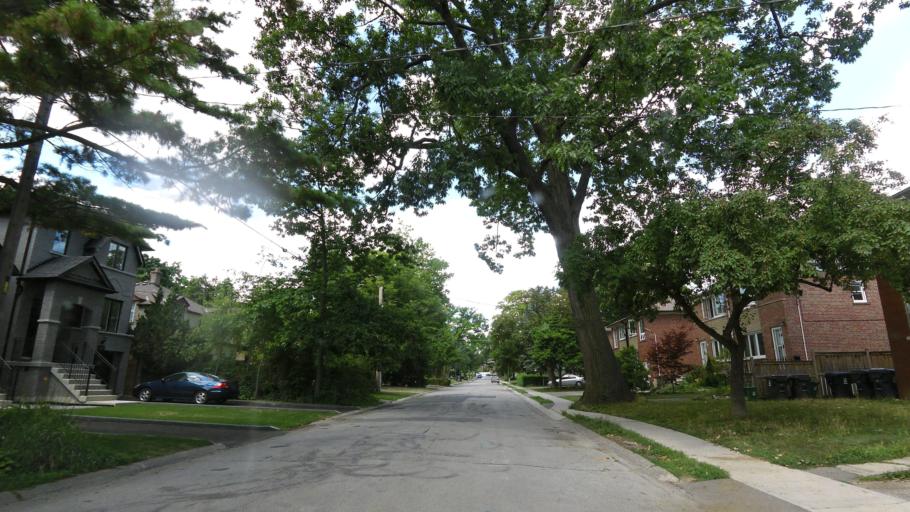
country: CA
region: Ontario
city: Etobicoke
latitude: 43.5912
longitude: -79.5343
